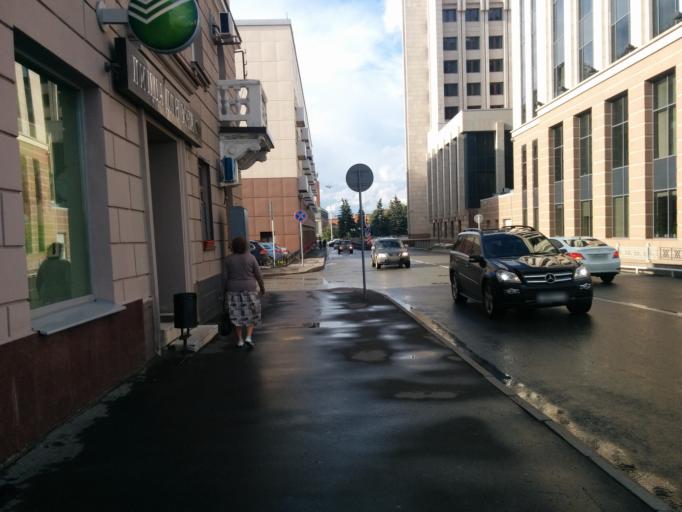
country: RU
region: Tatarstan
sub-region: Gorod Kazan'
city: Kazan
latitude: 55.7978
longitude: 49.1255
